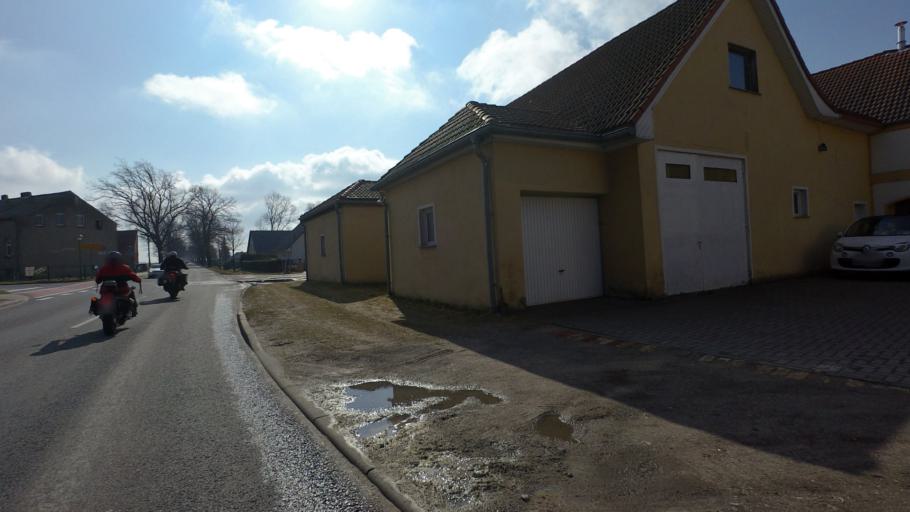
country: DE
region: Brandenburg
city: Glienicke
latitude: 52.6562
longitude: 13.3425
